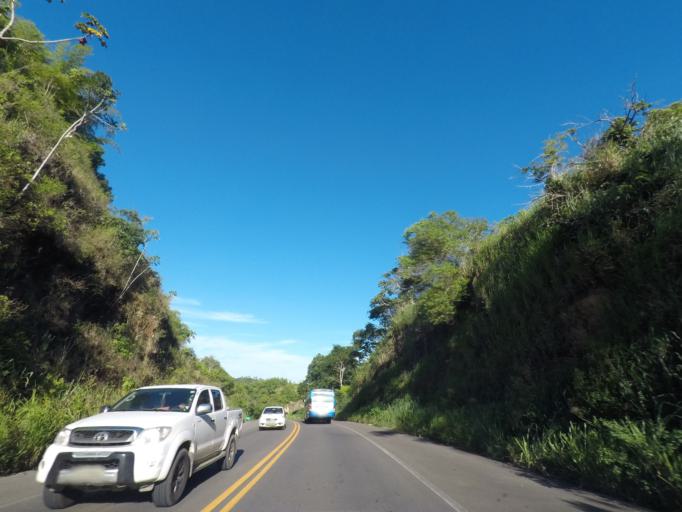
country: BR
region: Bahia
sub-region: Nazare
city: Nazare
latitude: -13.0288
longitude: -39.0041
